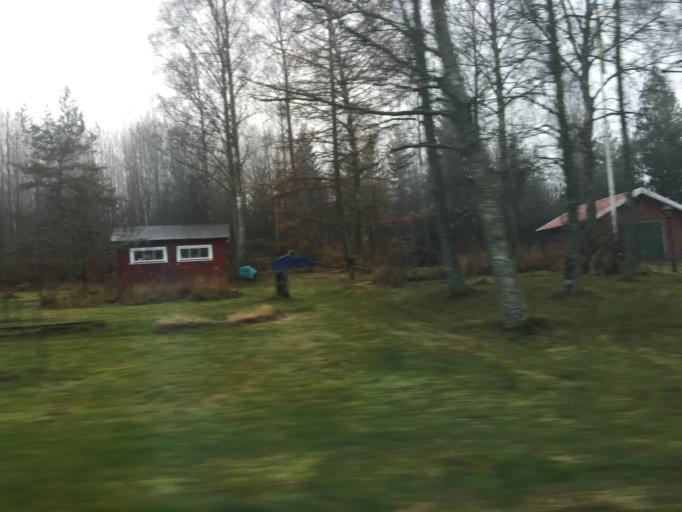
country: SE
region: Stockholm
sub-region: Botkyrka Kommun
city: Tullinge
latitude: 59.1054
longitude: 17.8780
